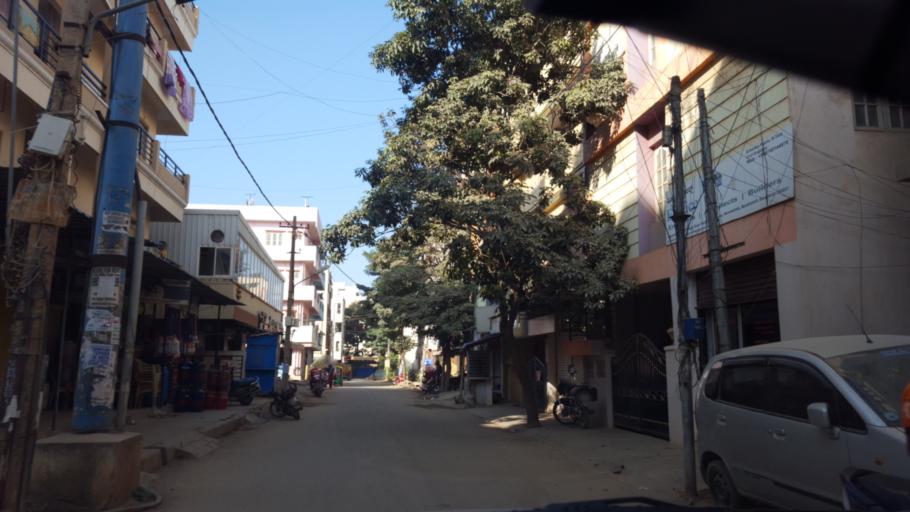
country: IN
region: Karnataka
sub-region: Bangalore Urban
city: Bangalore
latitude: 12.9498
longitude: 77.7092
